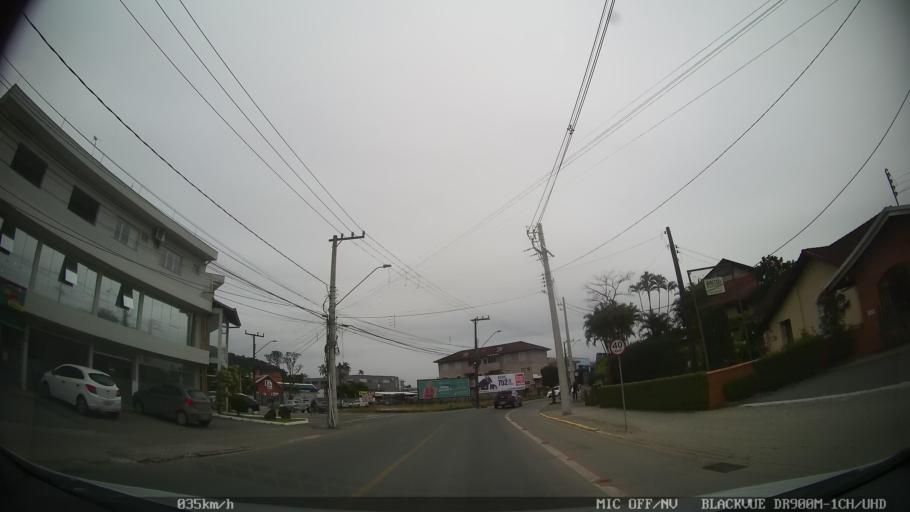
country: BR
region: Santa Catarina
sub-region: Joinville
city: Joinville
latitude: -26.2100
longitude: -48.9070
